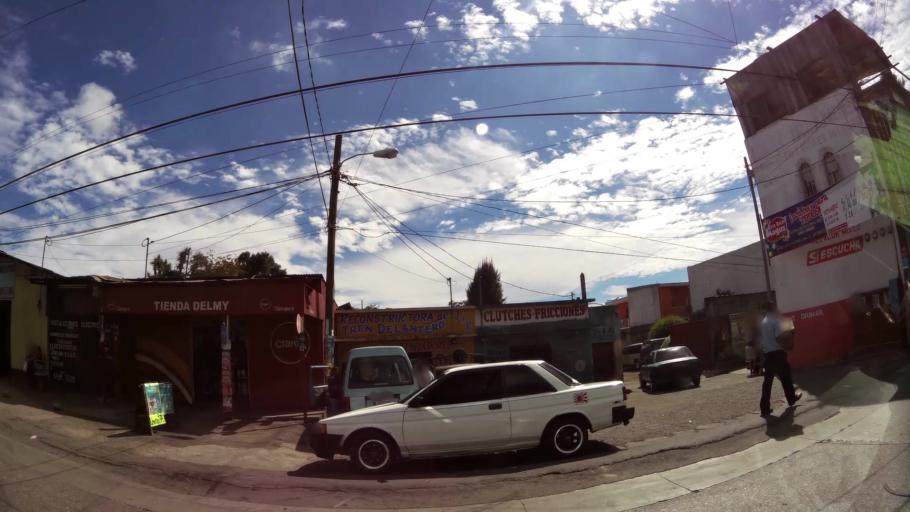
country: GT
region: Guatemala
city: Mixco
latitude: 14.6487
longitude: -90.5906
